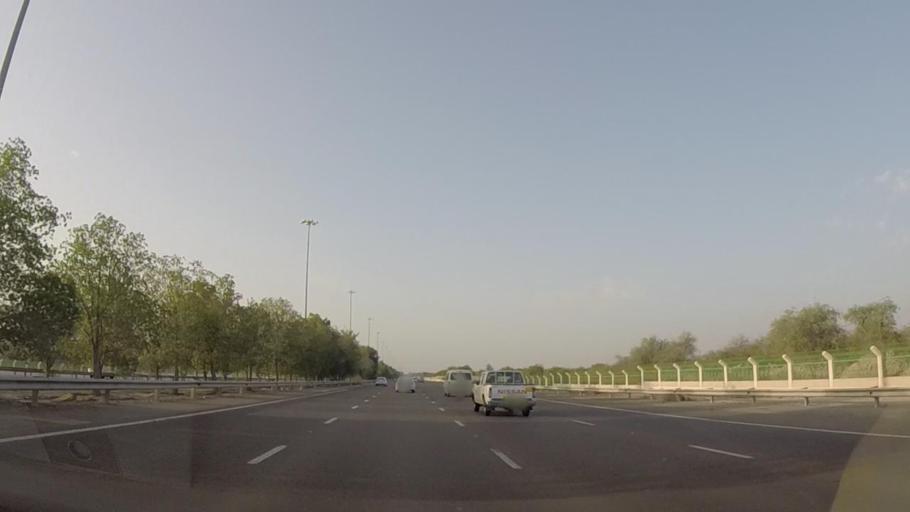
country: AE
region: Dubai
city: Dubai
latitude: 24.8497
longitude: 54.8961
